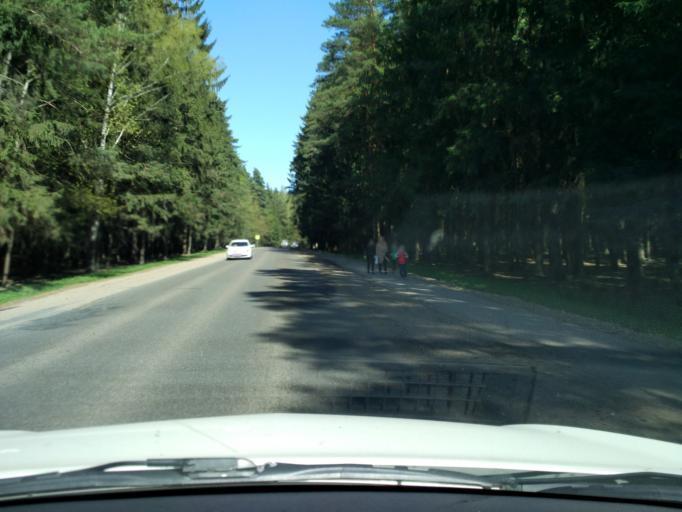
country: BY
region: Minsk
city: Lyasny
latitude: 53.9991
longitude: 27.6943
